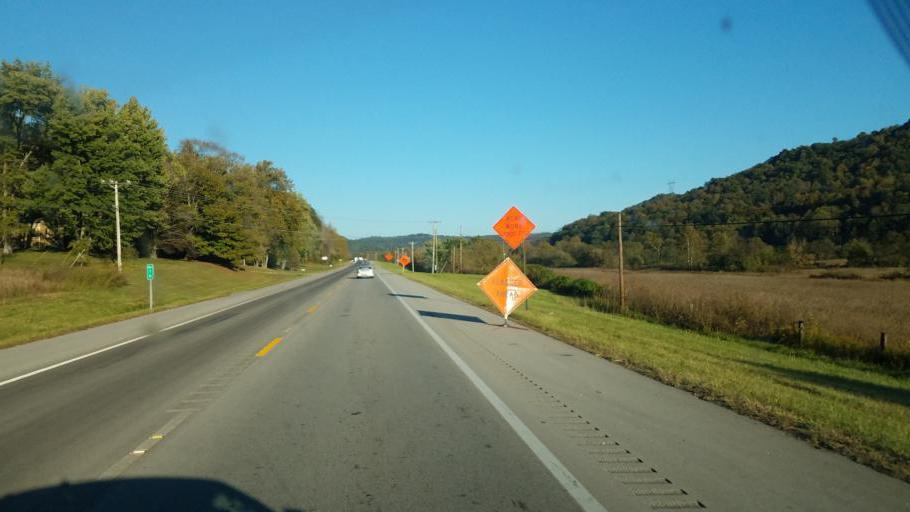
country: US
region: Kentucky
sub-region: Lewis County
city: Vanceburg
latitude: 38.5863
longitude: -83.3945
